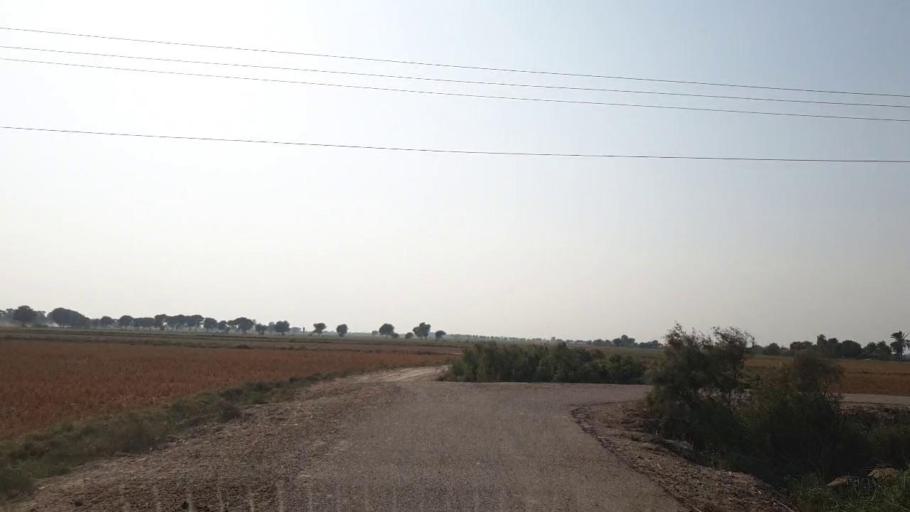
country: PK
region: Sindh
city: Bulri
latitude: 24.9914
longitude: 68.3734
